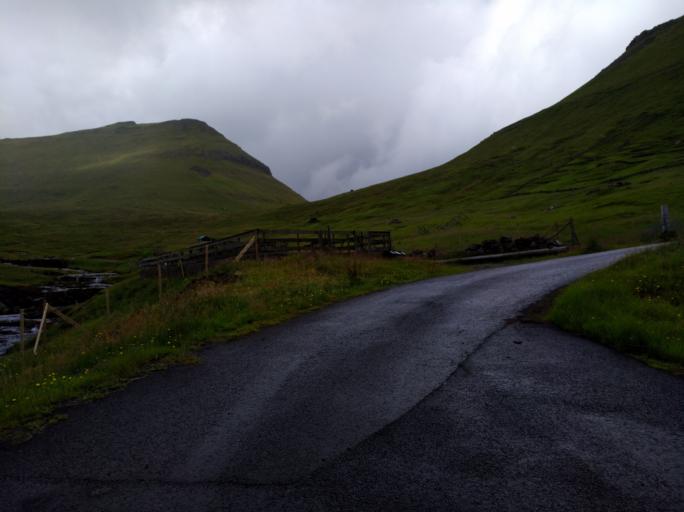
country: FO
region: Eysturoy
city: Fuglafjordur
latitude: 62.2793
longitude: -6.8612
